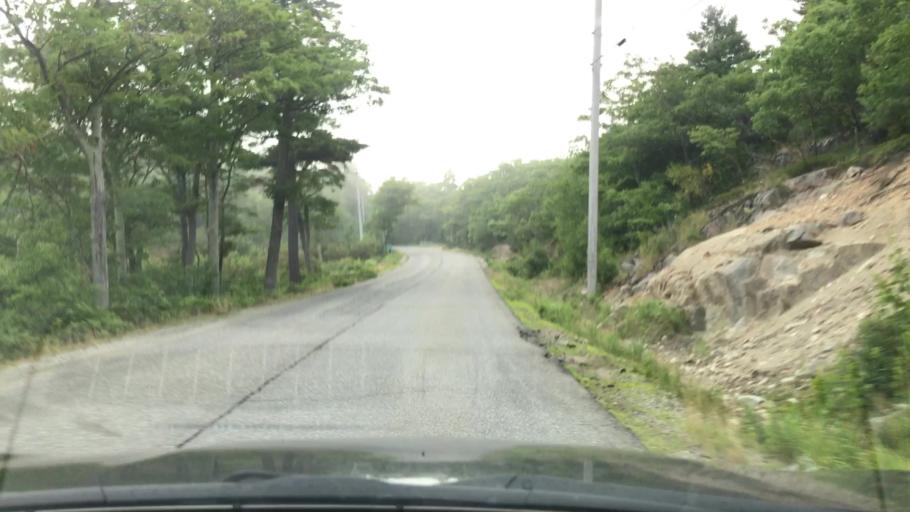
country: US
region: Maine
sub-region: Hancock County
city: Bar Harbor
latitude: 44.3543
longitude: -68.1845
